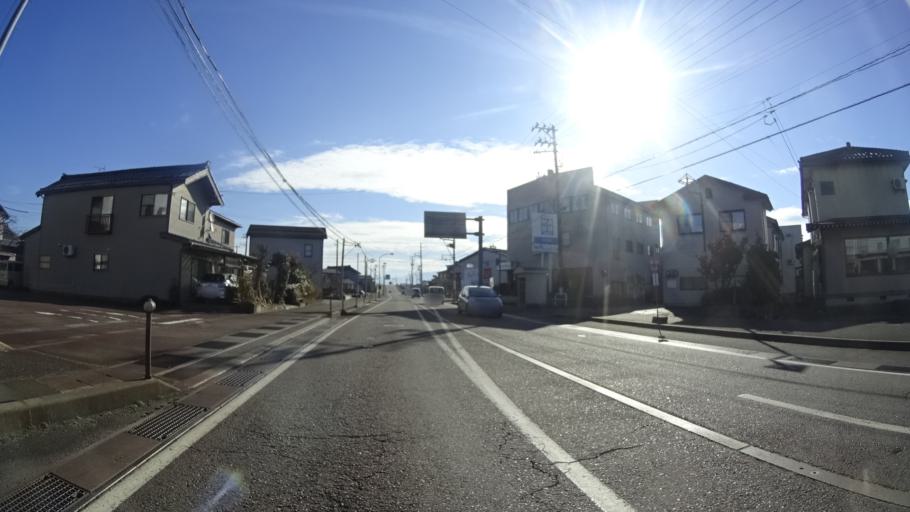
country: JP
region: Niigata
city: Mitsuke
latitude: 37.5474
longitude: 138.8773
